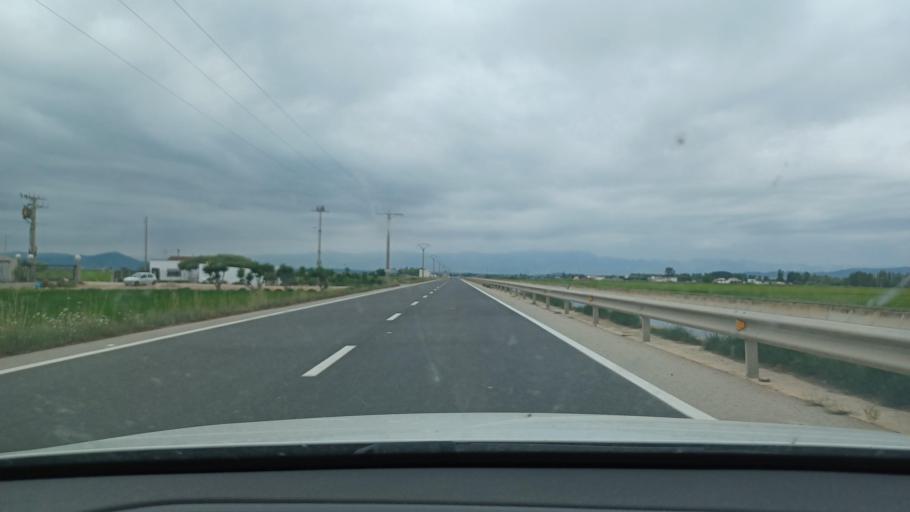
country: ES
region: Catalonia
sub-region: Provincia de Tarragona
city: Deltebre
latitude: 40.7083
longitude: 0.6921
